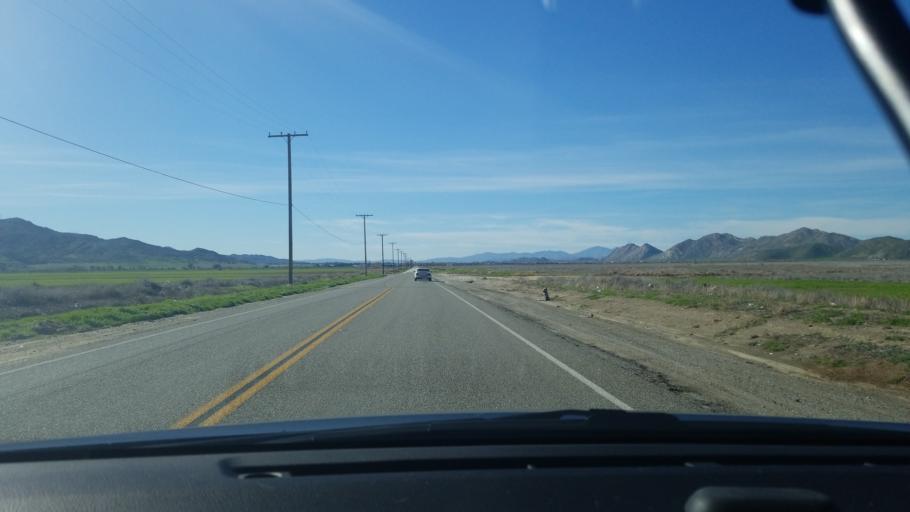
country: US
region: California
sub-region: Riverside County
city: Lakeview
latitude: 33.8668
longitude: -117.0490
